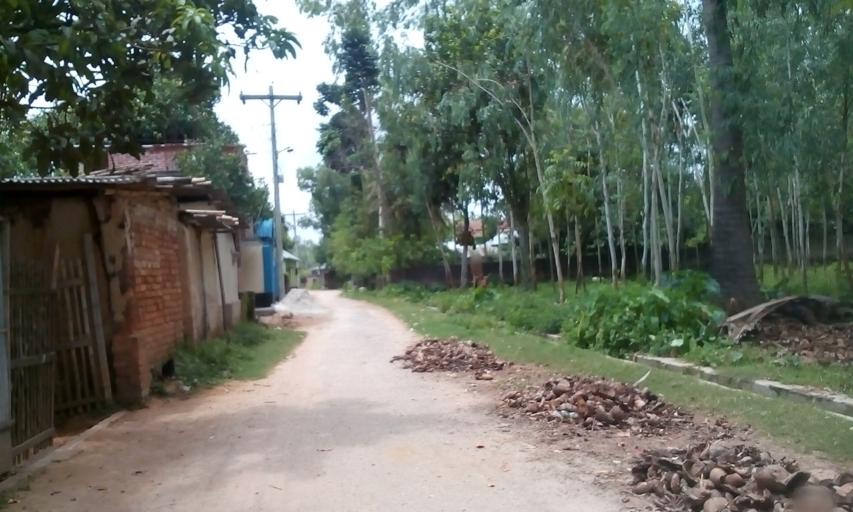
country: BD
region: Rangpur Division
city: Parbatipur
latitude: 25.3997
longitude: 88.9897
